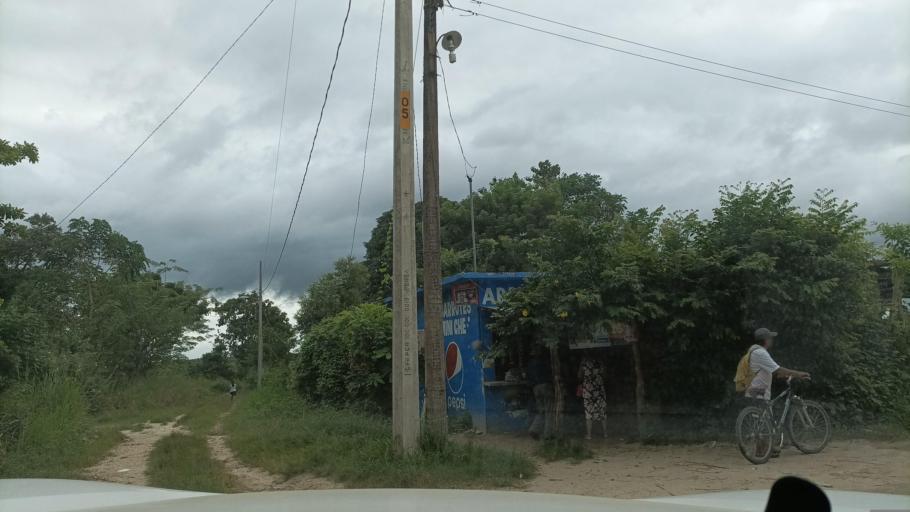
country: MX
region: Veracruz
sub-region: Cosoleacaque
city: Coacotla
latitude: 17.9439
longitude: -94.7056
